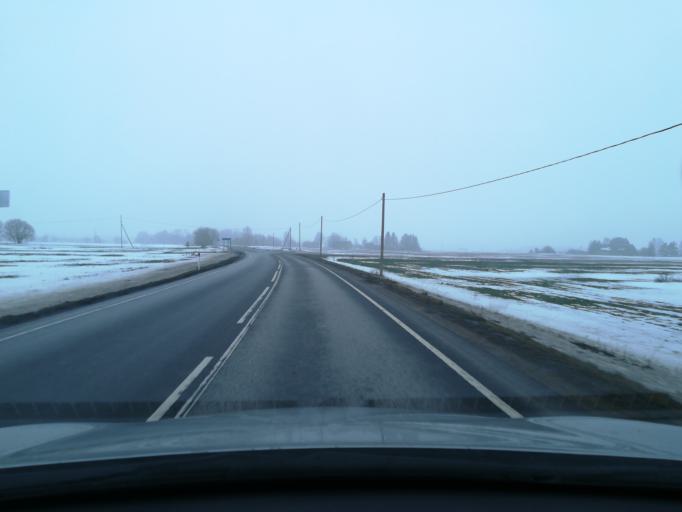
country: EE
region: Harju
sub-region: Raasiku vald
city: Raasiku
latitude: 59.3543
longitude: 25.1457
